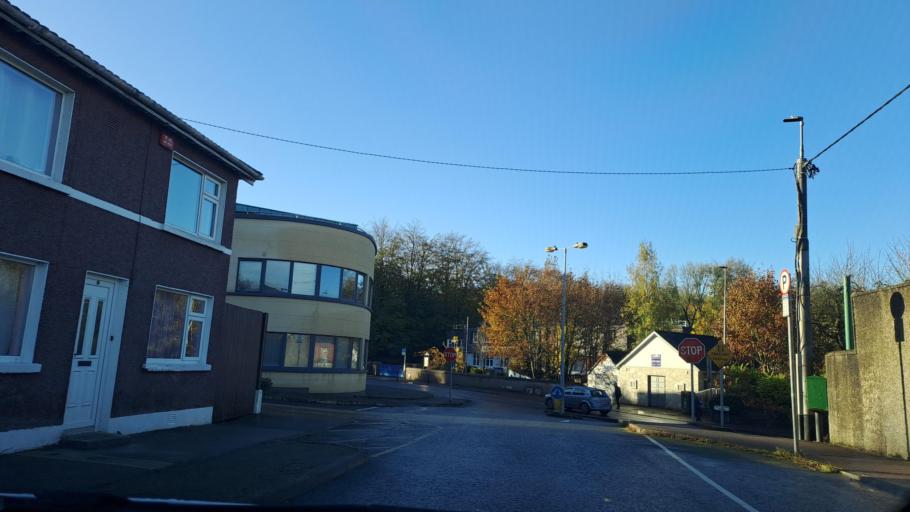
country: IE
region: Ulster
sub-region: County Monaghan
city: Monaghan
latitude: 54.2431
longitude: -6.9704
